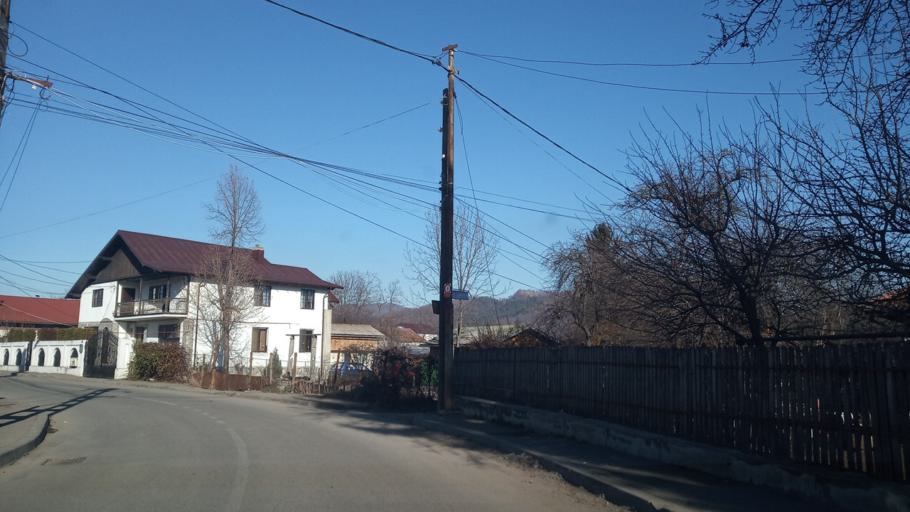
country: RO
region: Prahova
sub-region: Oras Breaza
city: Breaza
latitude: 45.1857
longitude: 25.6672
